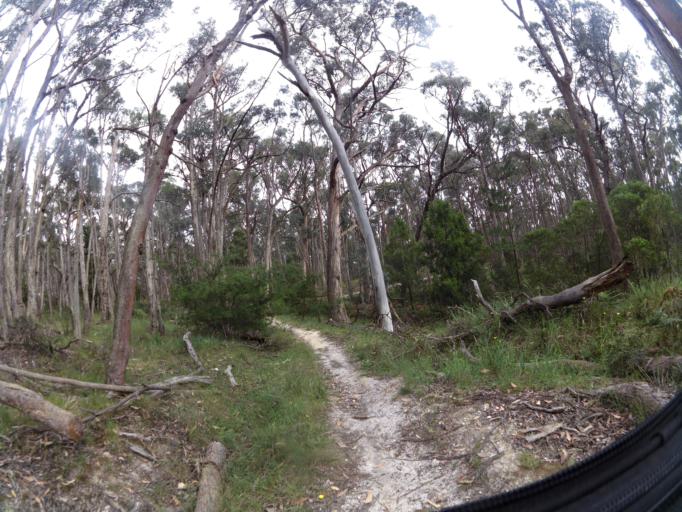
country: AU
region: Victoria
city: Brown Hill
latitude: -37.4759
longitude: 143.9121
